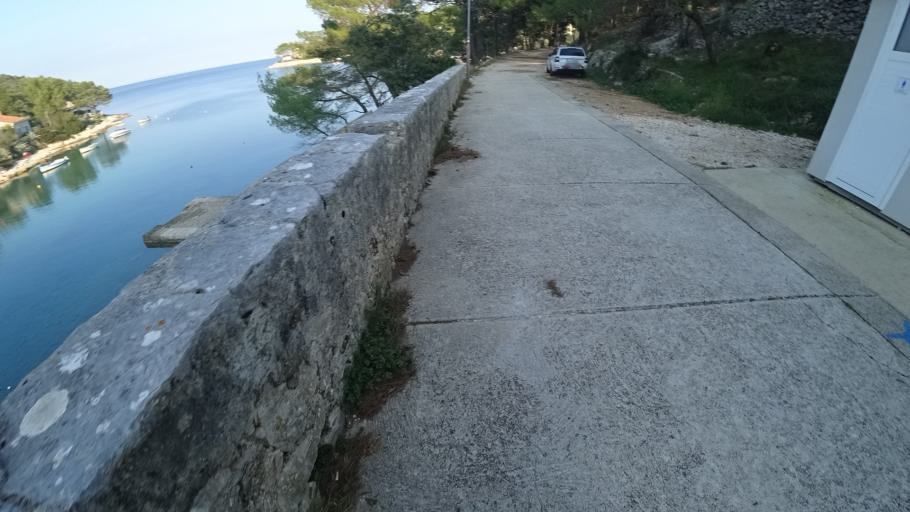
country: HR
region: Primorsko-Goranska
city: Mali Losinj
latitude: 44.5269
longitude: 14.4804
